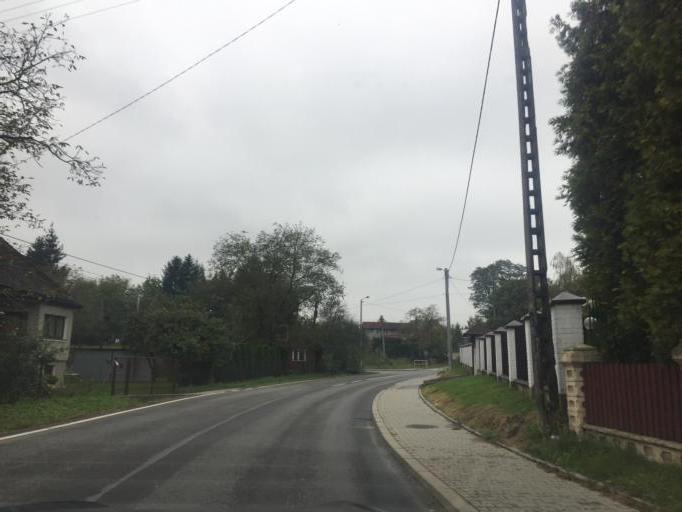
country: PL
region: Lesser Poland Voivodeship
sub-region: Powiat wielicki
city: Wieliczka
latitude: 49.9908
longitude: 20.0258
